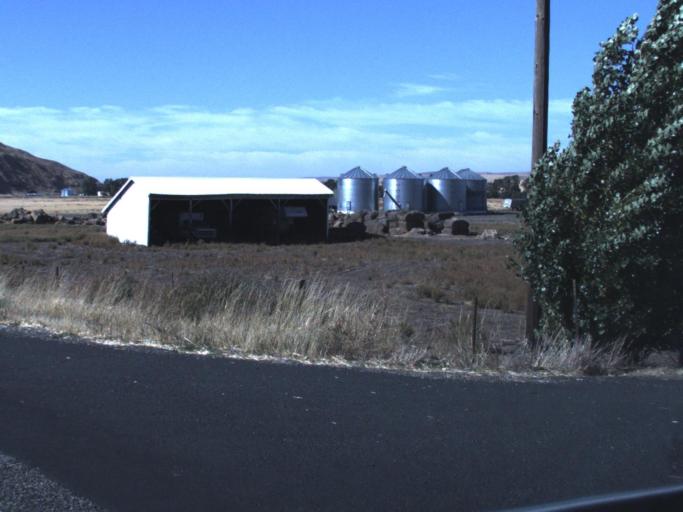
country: US
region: Washington
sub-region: Walla Walla County
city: Waitsburg
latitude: 46.2666
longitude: -118.2083
